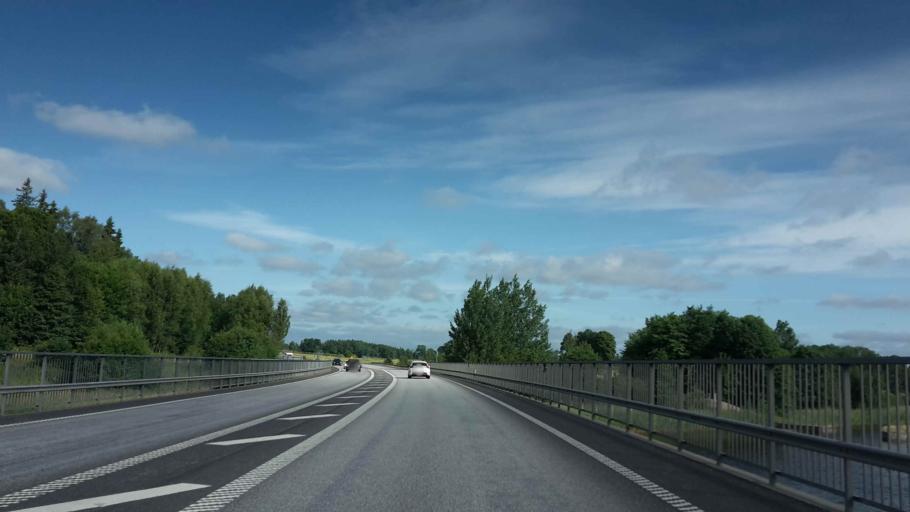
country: SE
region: OErebro
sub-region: Askersunds Kommun
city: Askersund
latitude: 58.8377
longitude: 14.9288
